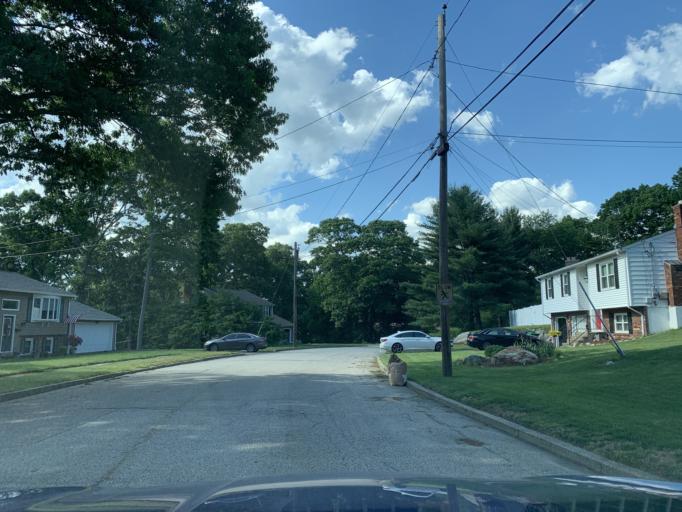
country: US
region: Rhode Island
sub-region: Kent County
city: East Greenwich
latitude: 41.6797
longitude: -71.4645
